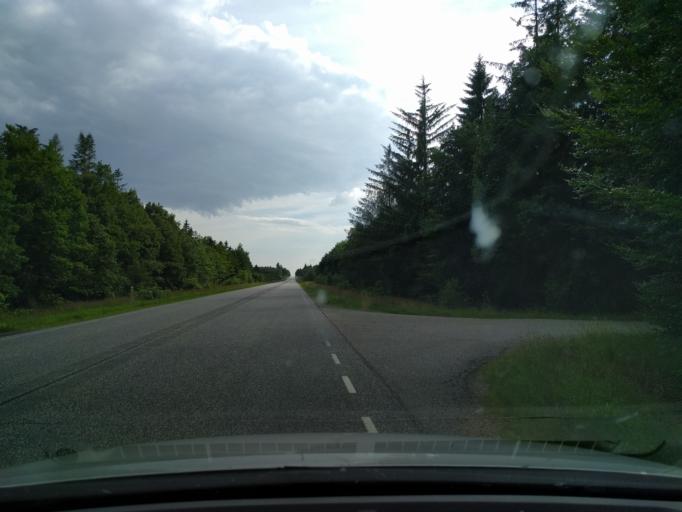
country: DK
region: Central Jutland
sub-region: Herning Kommune
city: Kibaek
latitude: 56.0658
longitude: 8.9009
